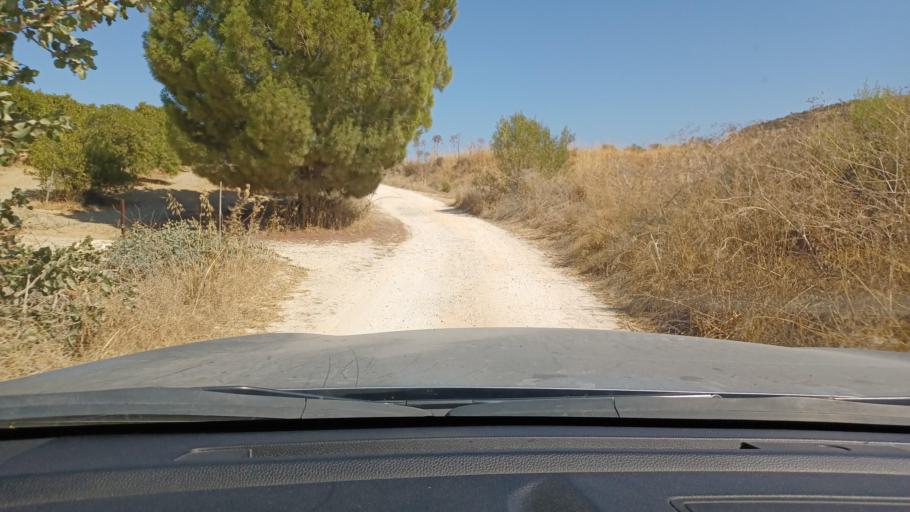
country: CY
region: Pafos
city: Polis
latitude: 35.0211
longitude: 32.4474
